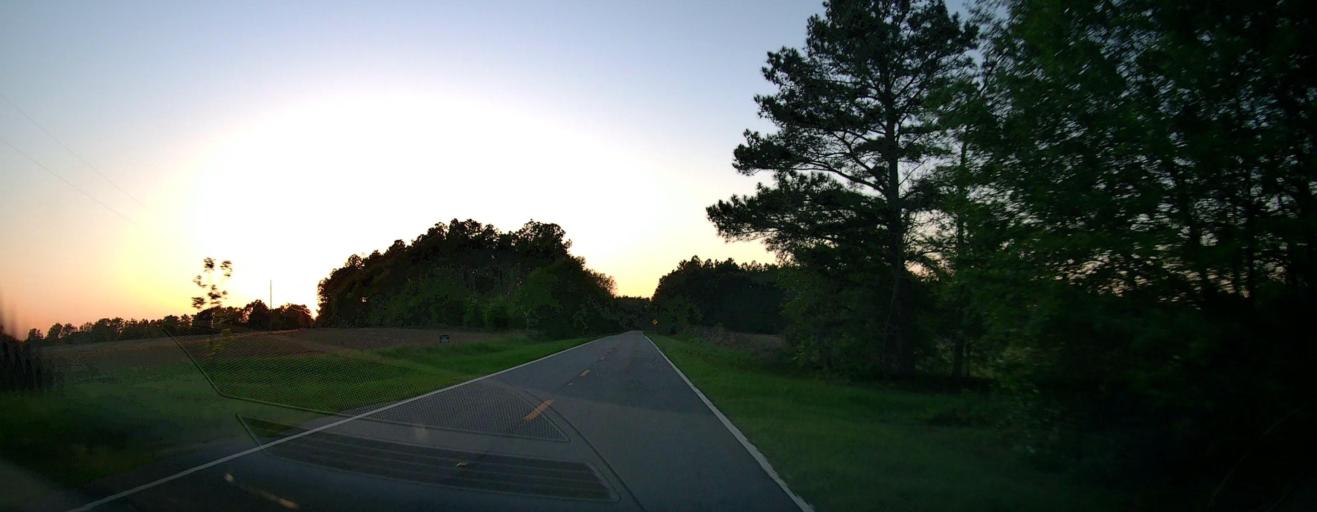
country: US
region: Georgia
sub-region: Wilcox County
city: Rochelle
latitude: 31.7929
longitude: -83.4395
